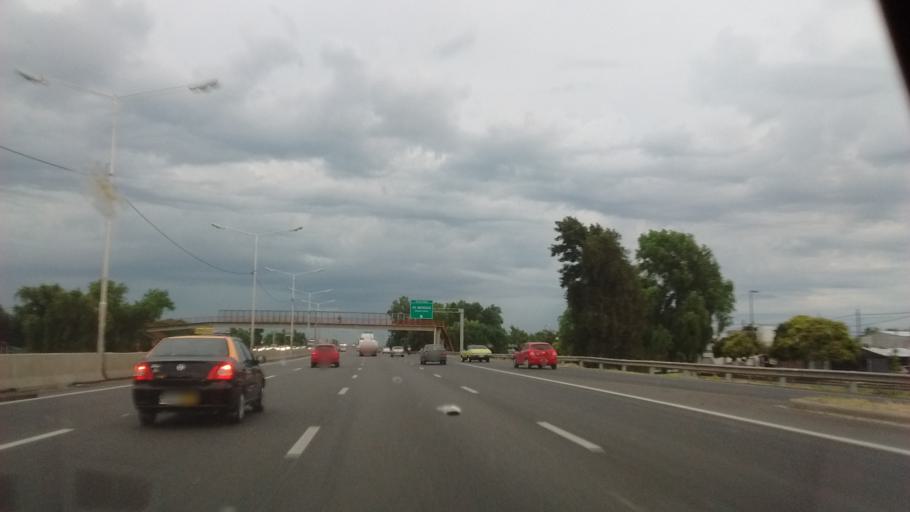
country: AR
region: Santa Fe
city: Perez
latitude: -32.9469
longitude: -60.7220
